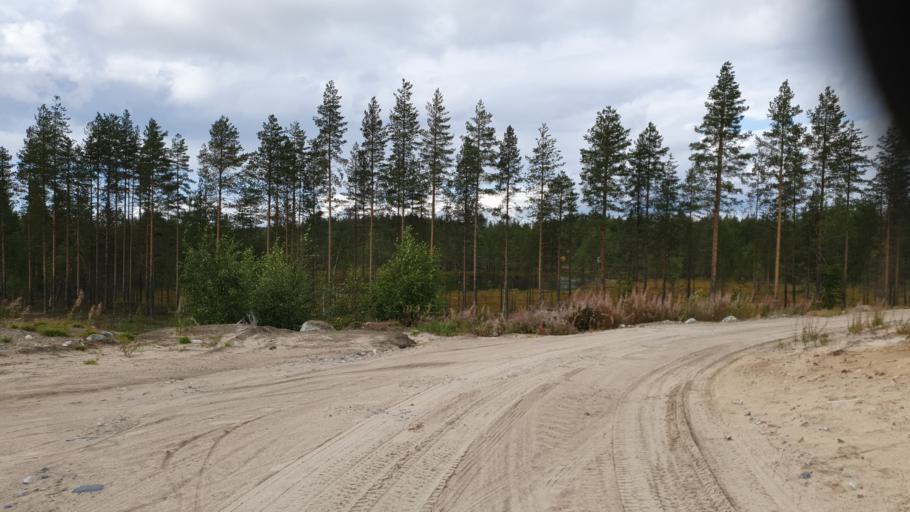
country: FI
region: Kainuu
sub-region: Kehys-Kainuu
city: Kuhmo
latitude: 64.1503
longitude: 29.3698
